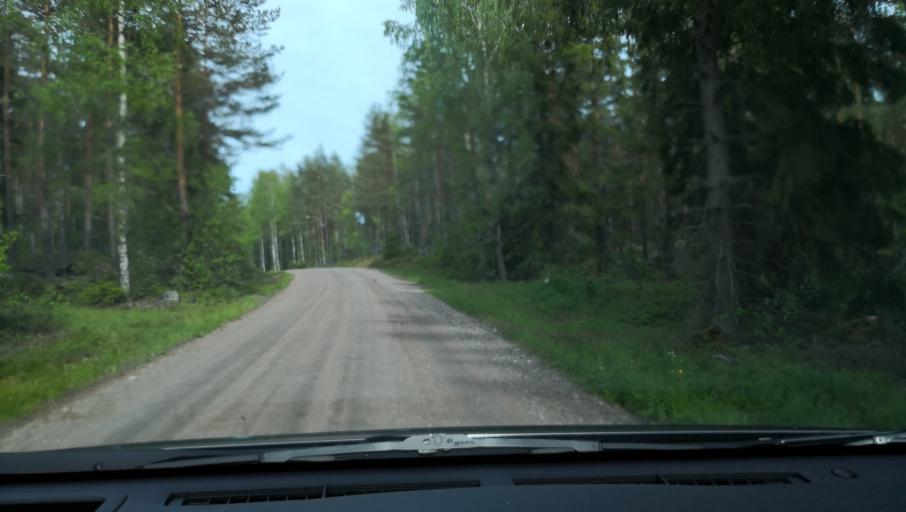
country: SE
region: Vaestmanland
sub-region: Arboga Kommun
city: Tyringe
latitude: 59.3631
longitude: 15.9757
